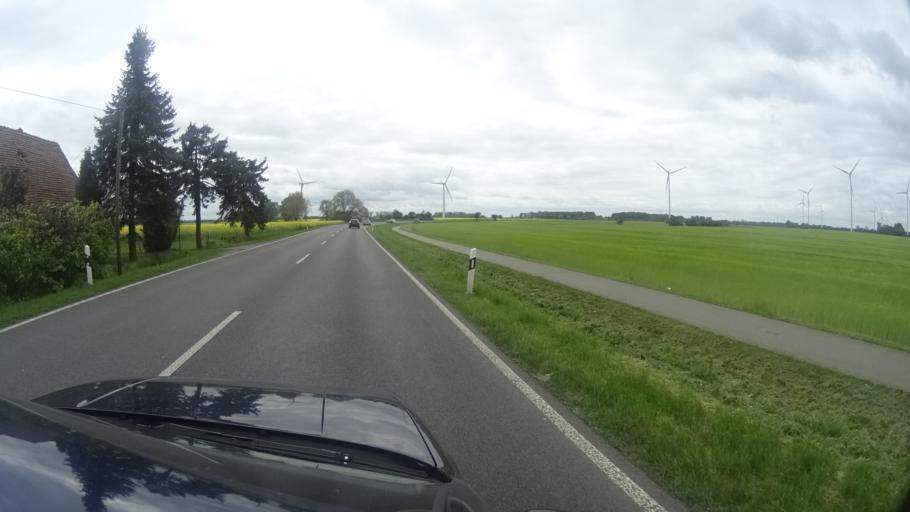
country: DE
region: Brandenburg
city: Dabergotz
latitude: 52.9068
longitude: 12.7575
